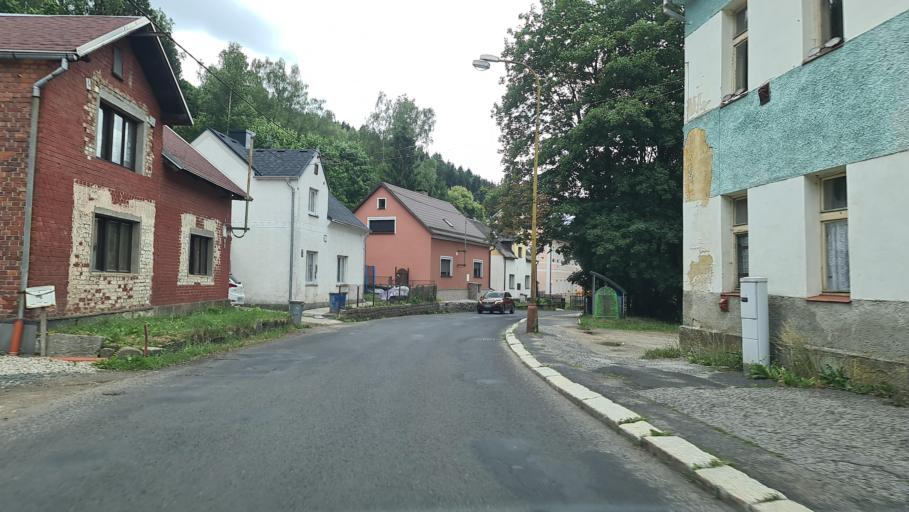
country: CZ
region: Karlovarsky
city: Kraslice
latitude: 50.3333
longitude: 12.5196
